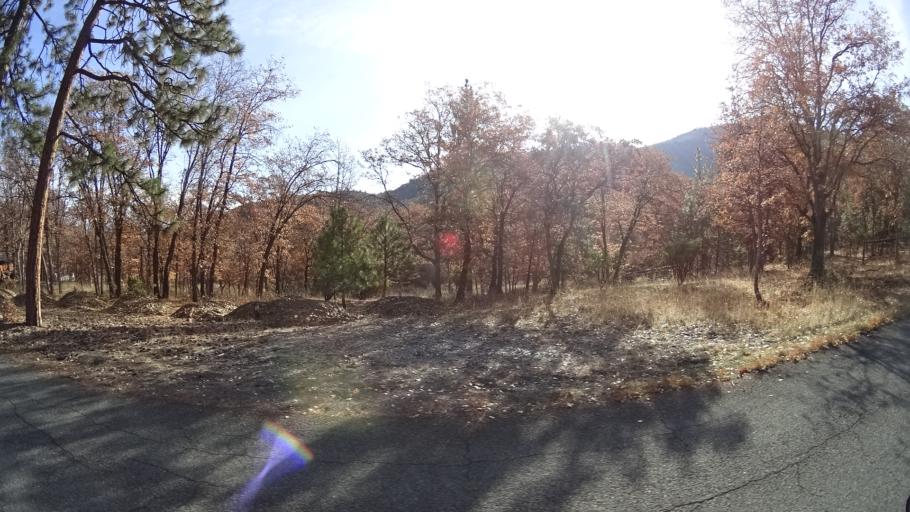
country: US
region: California
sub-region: Siskiyou County
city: Yreka
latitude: 41.6566
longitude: -122.6264
